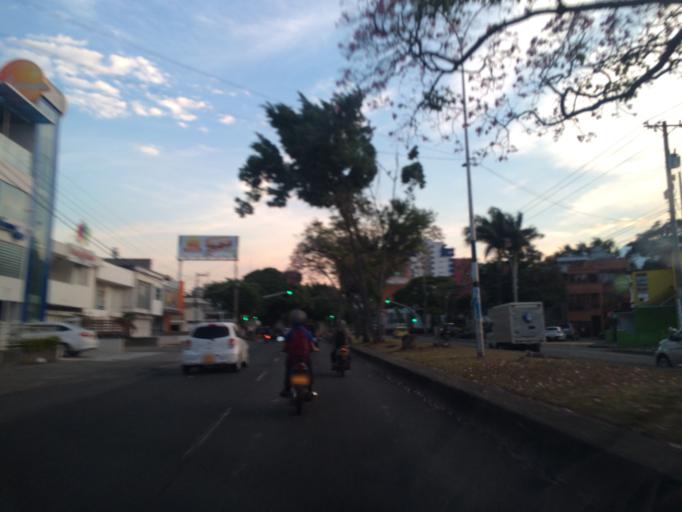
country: CO
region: Valle del Cauca
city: Cali
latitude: 3.4260
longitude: -76.5400
